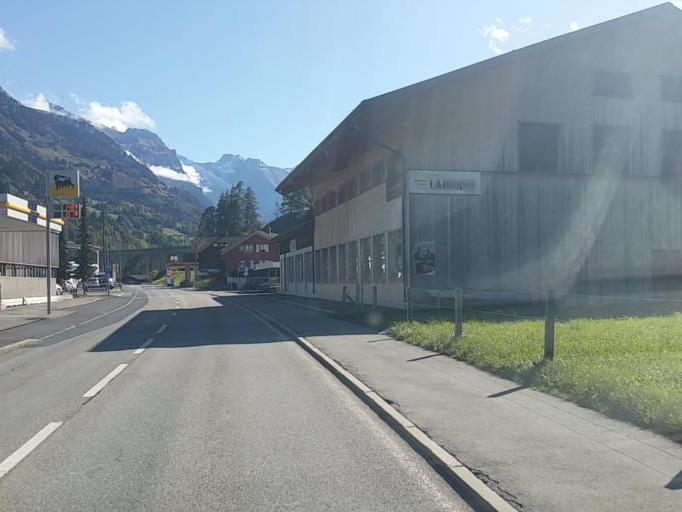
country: CH
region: Bern
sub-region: Frutigen-Niedersimmental District
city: Frutigen
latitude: 46.5797
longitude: 7.6513
